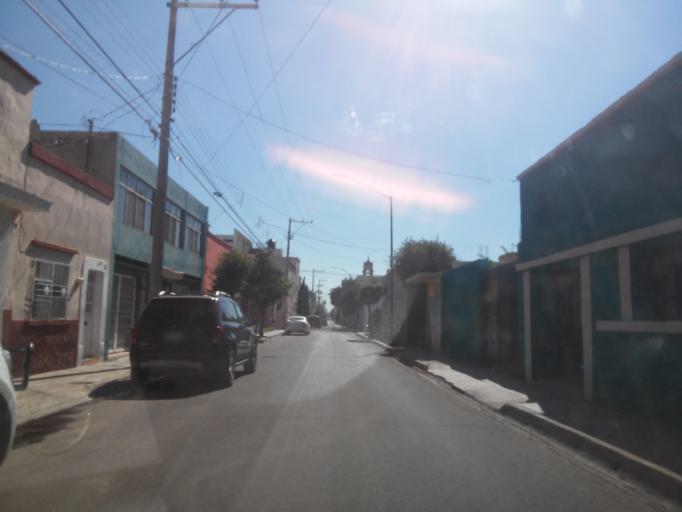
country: MX
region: Durango
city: Victoria de Durango
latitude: 24.0316
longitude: -104.6680
